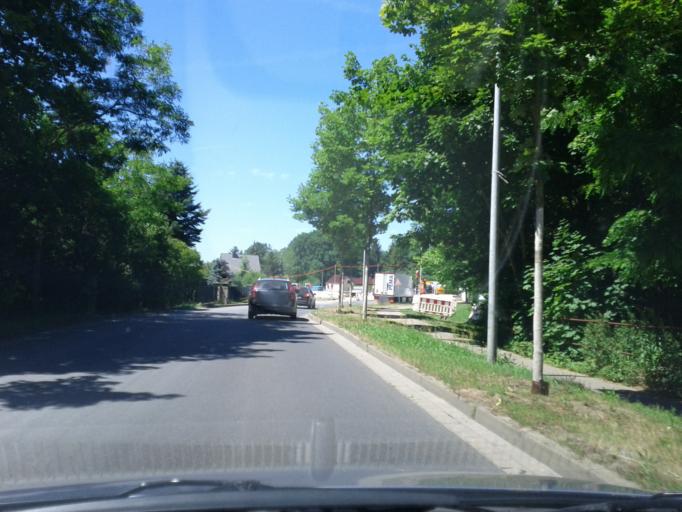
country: DE
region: Brandenburg
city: Langewahl
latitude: 52.3378
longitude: 14.0756
